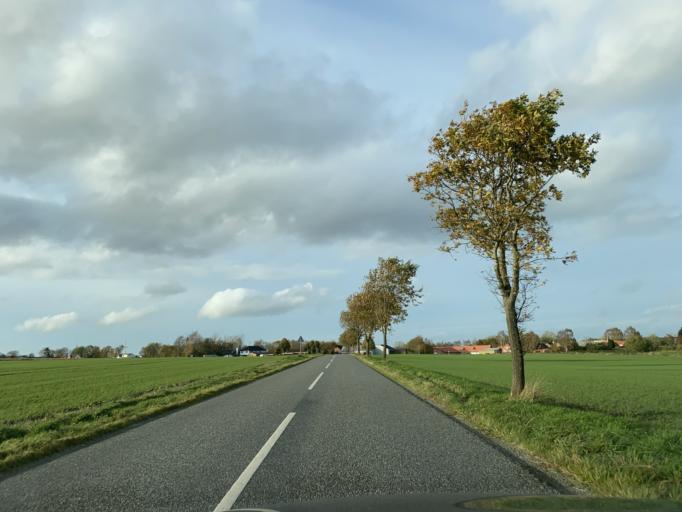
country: DK
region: Central Jutland
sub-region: Viborg Kommune
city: Bjerringbro
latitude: 56.2491
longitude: 9.7125
